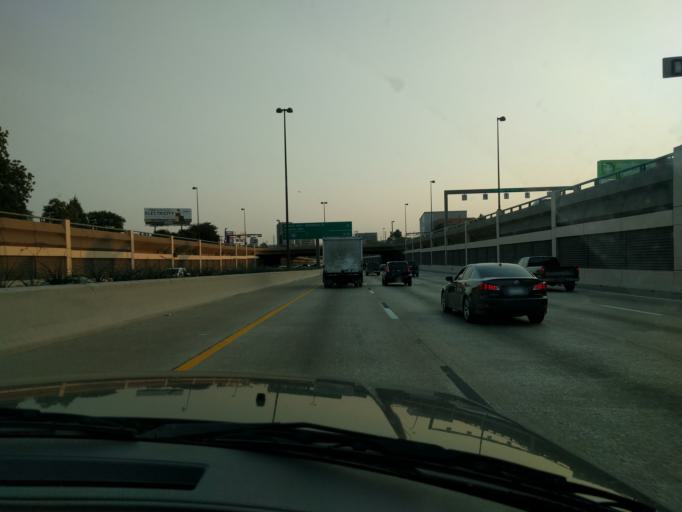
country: US
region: Texas
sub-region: Dallas County
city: Highland Park
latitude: 32.8235
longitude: -96.7853
